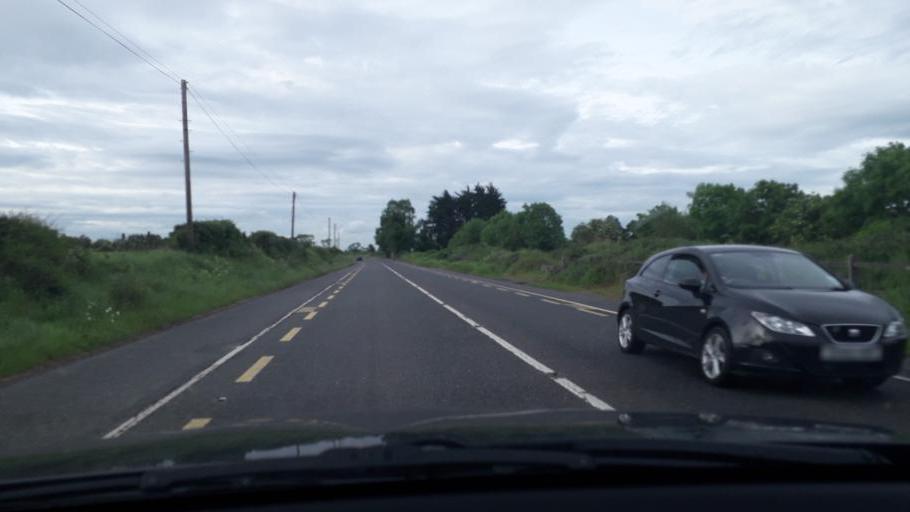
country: IE
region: Leinster
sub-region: County Carlow
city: Carlow
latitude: 52.7878
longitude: -6.9471
